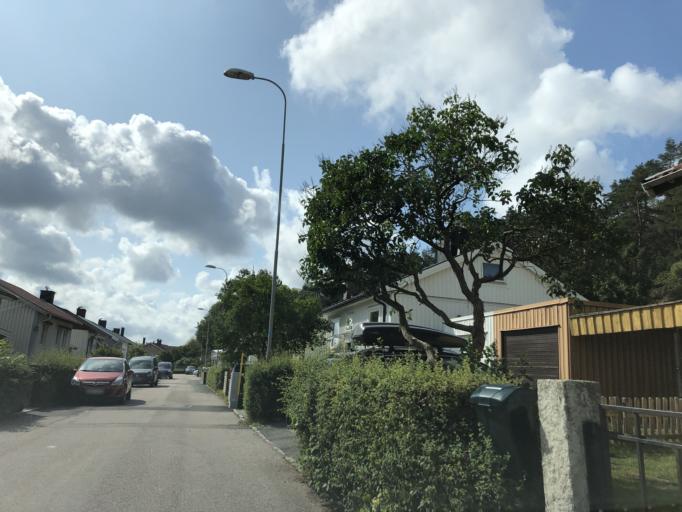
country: SE
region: Vaestra Goetaland
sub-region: Goteborg
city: Majorna
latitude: 57.7172
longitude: 11.8993
